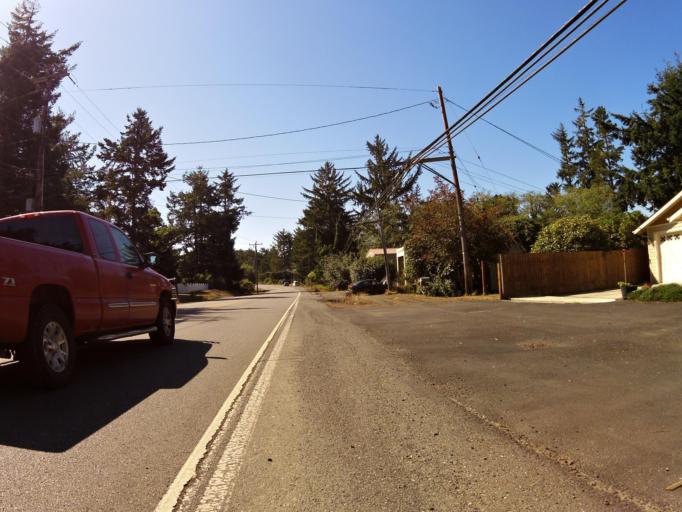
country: US
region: Oregon
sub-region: Coos County
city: Barview
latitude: 43.3565
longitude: -124.3103
